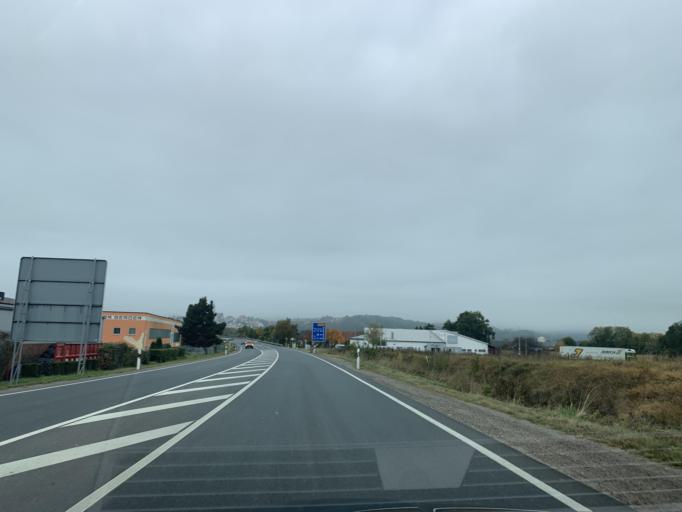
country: DE
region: Bavaria
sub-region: Upper Palatinate
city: Nabburg
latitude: 49.4557
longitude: 12.1998
